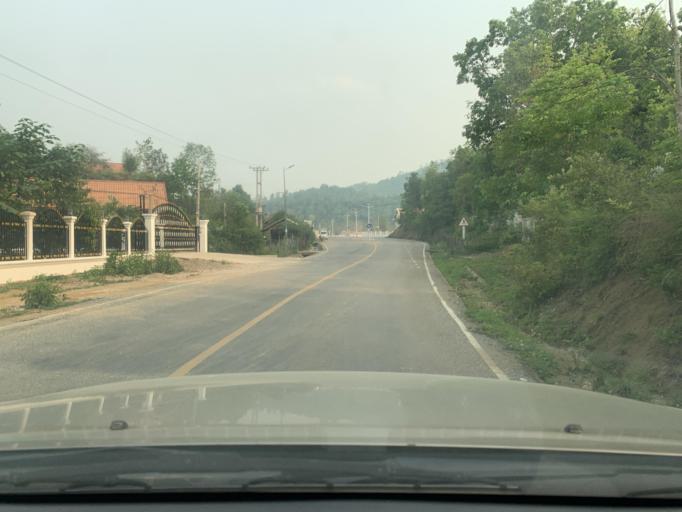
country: LA
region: Louangphabang
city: Louangphabang
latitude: 19.9084
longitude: 102.0847
